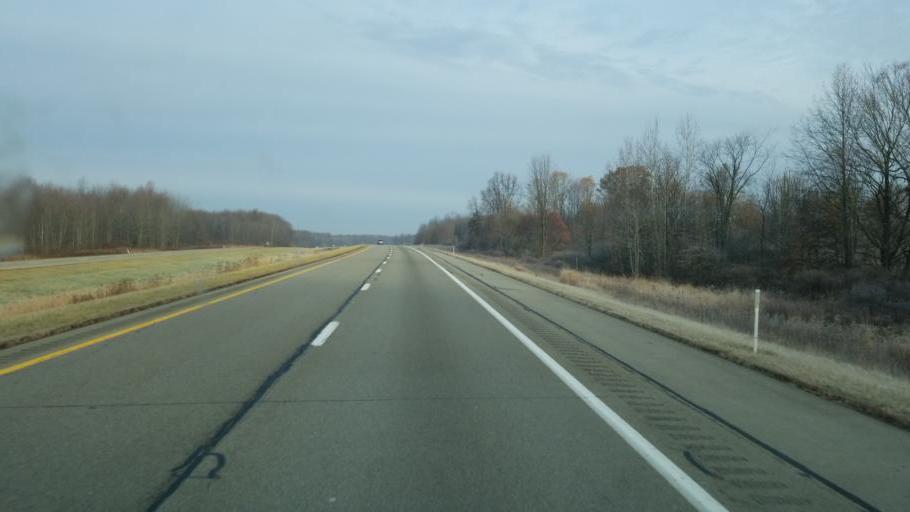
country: US
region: Pennsylvania
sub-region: Crawford County
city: Cochranton
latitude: 41.4980
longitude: -80.1675
